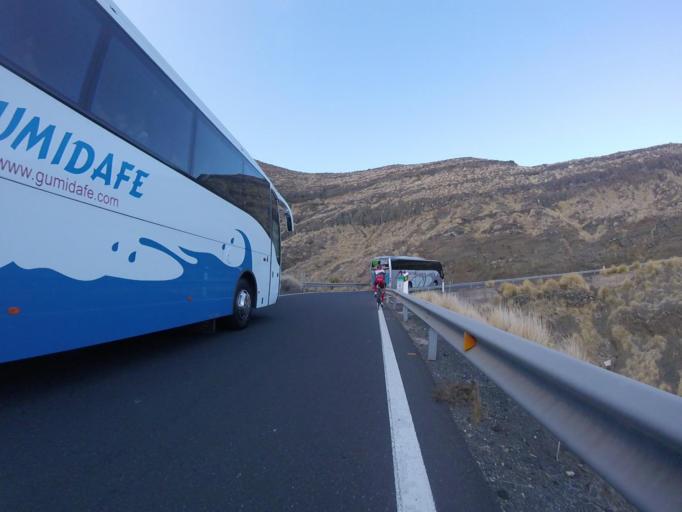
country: ES
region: Canary Islands
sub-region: Provincia de Las Palmas
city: Agaete
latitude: 28.0773
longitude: -15.7063
